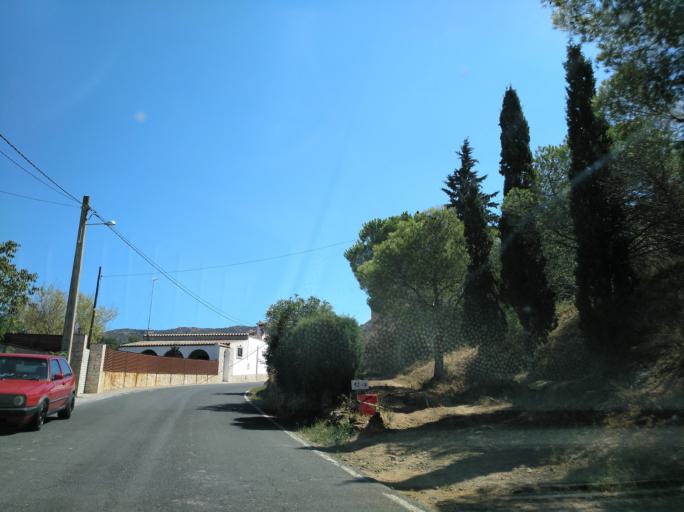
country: ES
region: Catalonia
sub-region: Provincia de Girona
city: Vilajuiga
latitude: 42.3278
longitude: 3.0973
